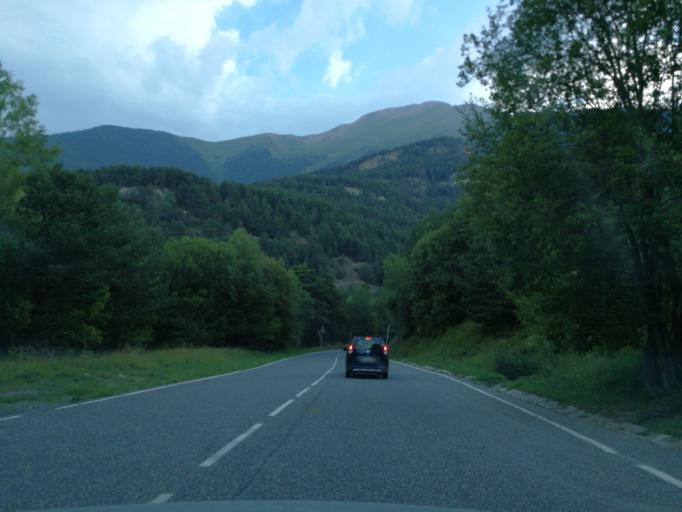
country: AD
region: Ordino
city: Ordino
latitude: 42.5567
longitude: 1.5485
